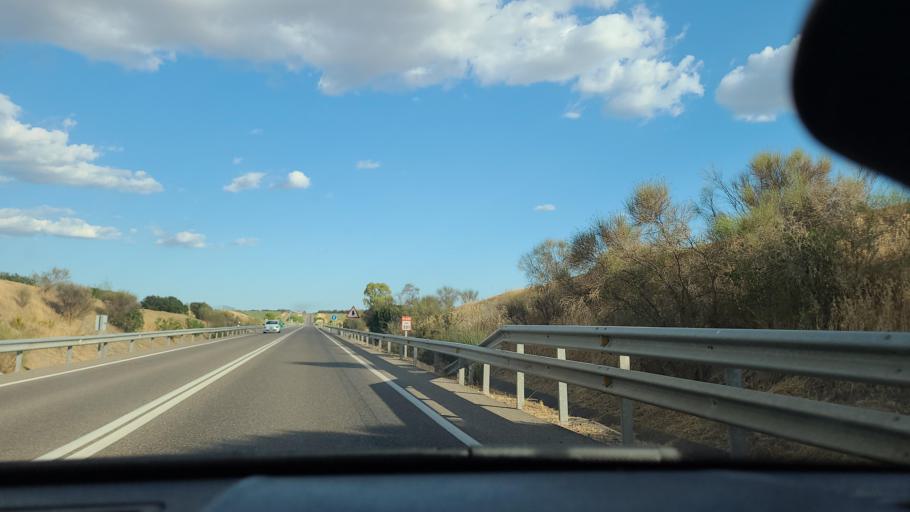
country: ES
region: Andalusia
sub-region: Province of Cordoba
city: Belmez
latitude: 38.2641
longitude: -5.1834
